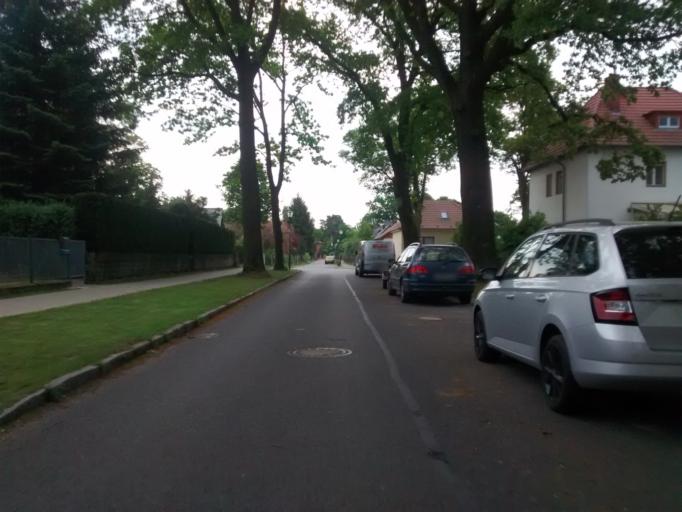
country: DE
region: Brandenburg
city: Hohen Neuendorf
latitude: 52.6663
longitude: 13.2758
